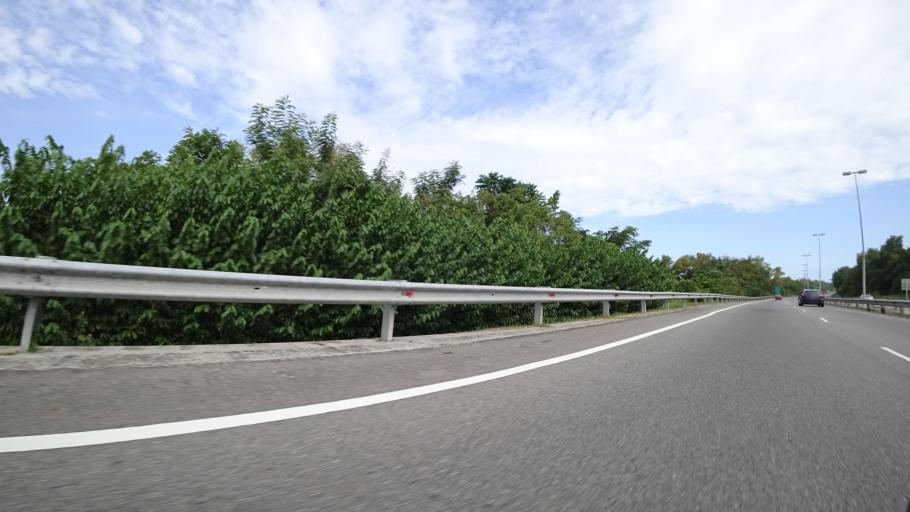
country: BN
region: Brunei and Muara
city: Bandar Seri Begawan
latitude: 4.9322
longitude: 114.9118
